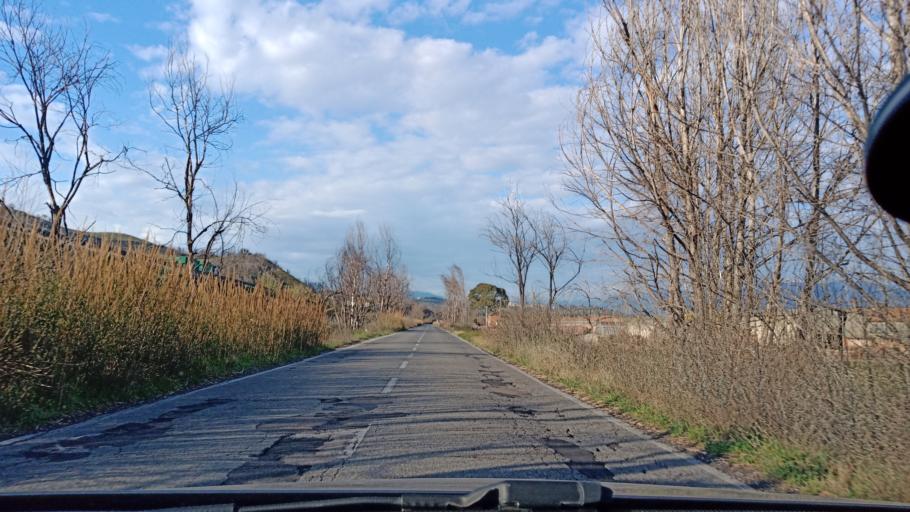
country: IT
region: Latium
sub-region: Citta metropolitana di Roma Capitale
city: Civitella San Paolo
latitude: 42.1905
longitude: 12.6040
